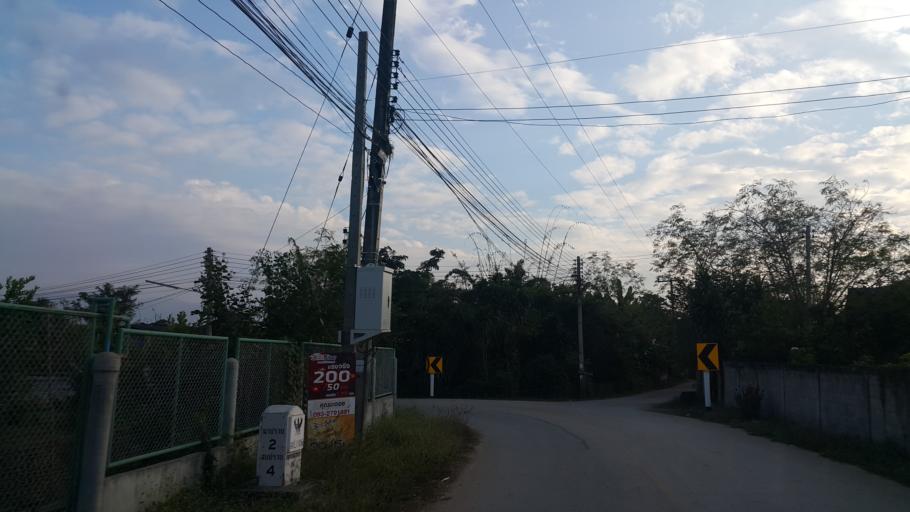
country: TH
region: Lampang
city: Sop Prap
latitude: 17.9020
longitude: 99.3287
